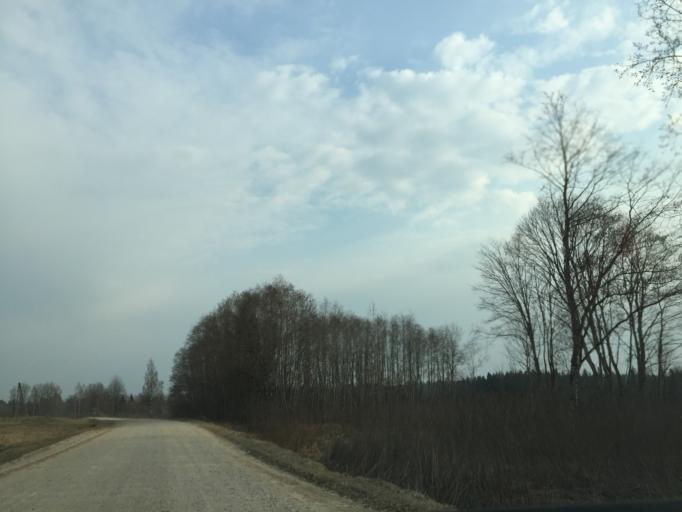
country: LV
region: Raunas
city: Rauna
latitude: 57.1583
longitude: 25.5754
